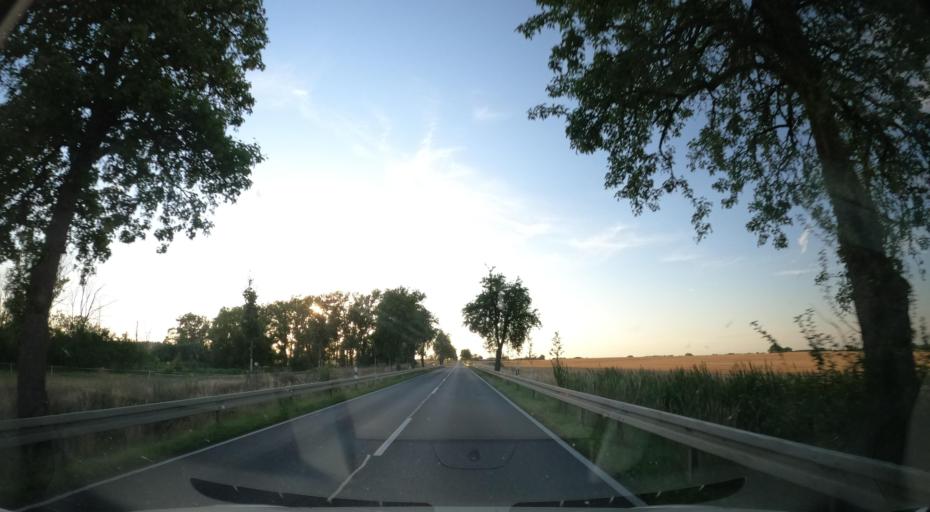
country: DE
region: Mecklenburg-Vorpommern
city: Viereck
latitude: 53.4869
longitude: 14.1015
